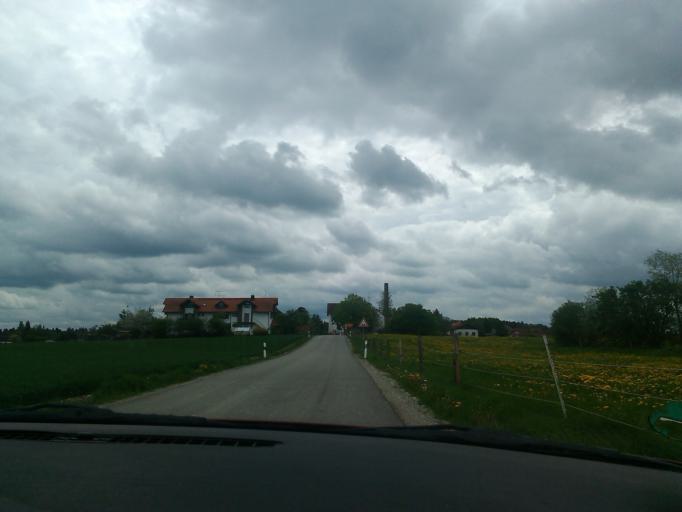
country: DE
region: Bavaria
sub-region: Upper Bavaria
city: Gauting
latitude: 48.0816
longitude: 11.3430
